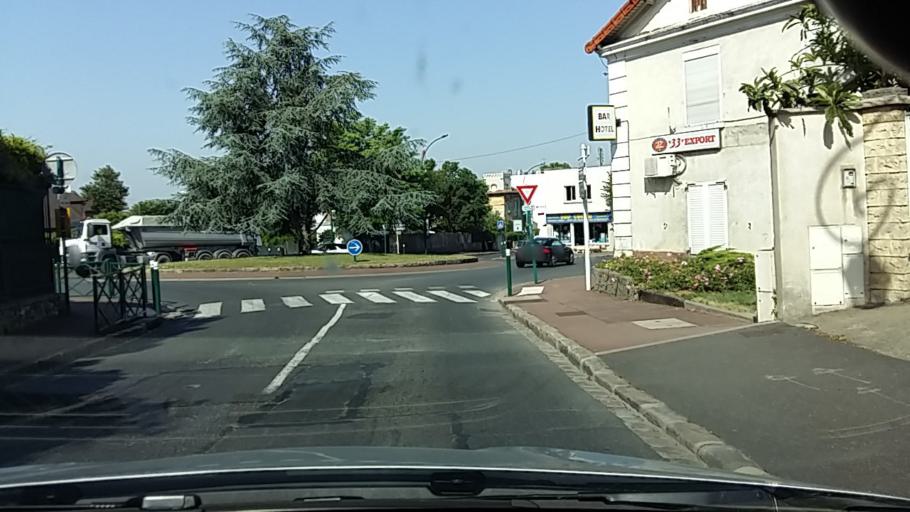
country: FR
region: Ile-de-France
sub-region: Departement du Val-de-Marne
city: Boissy-Saint-Leger
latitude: 48.7692
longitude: 2.5128
